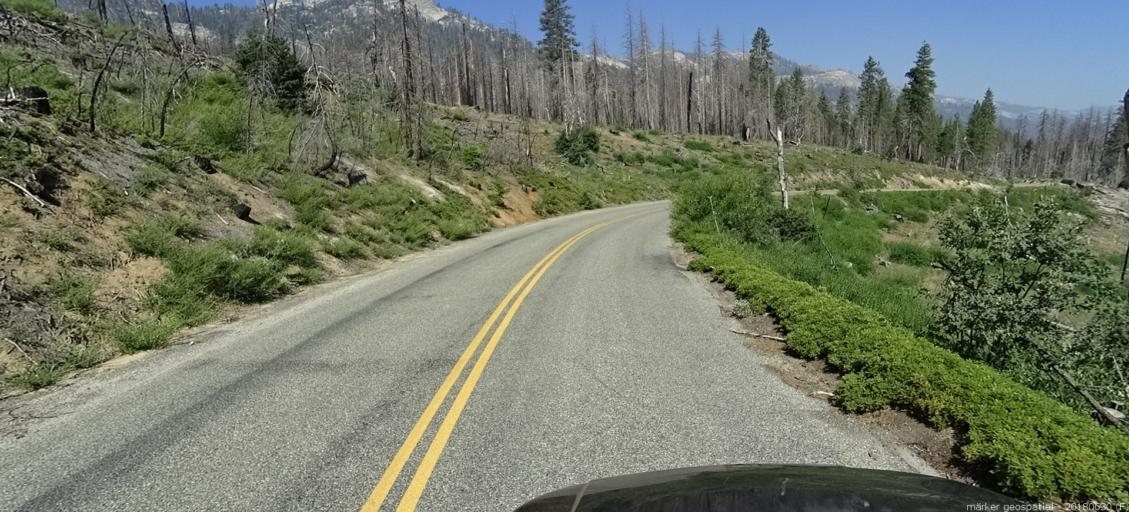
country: US
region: California
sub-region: Madera County
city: Oakhurst
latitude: 37.3367
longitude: -119.3712
